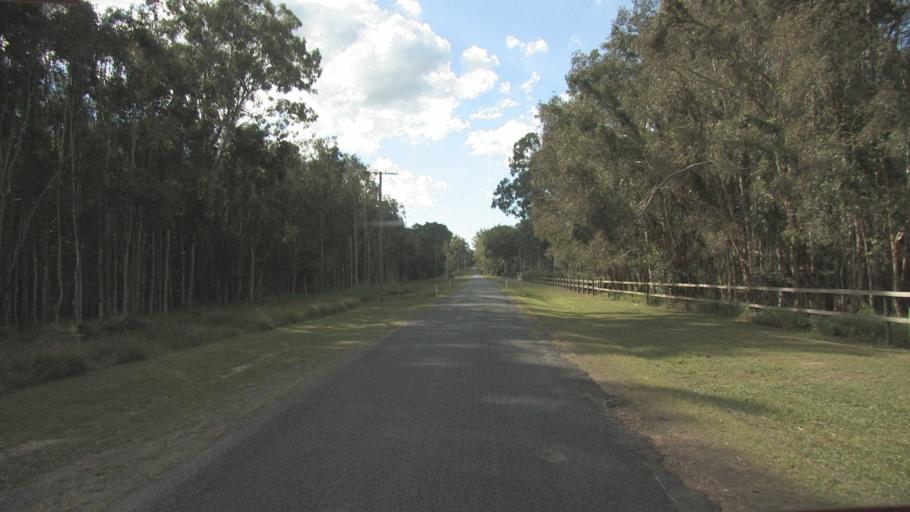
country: AU
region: Queensland
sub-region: Gold Coast
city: Yatala
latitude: -27.6637
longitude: 153.2410
